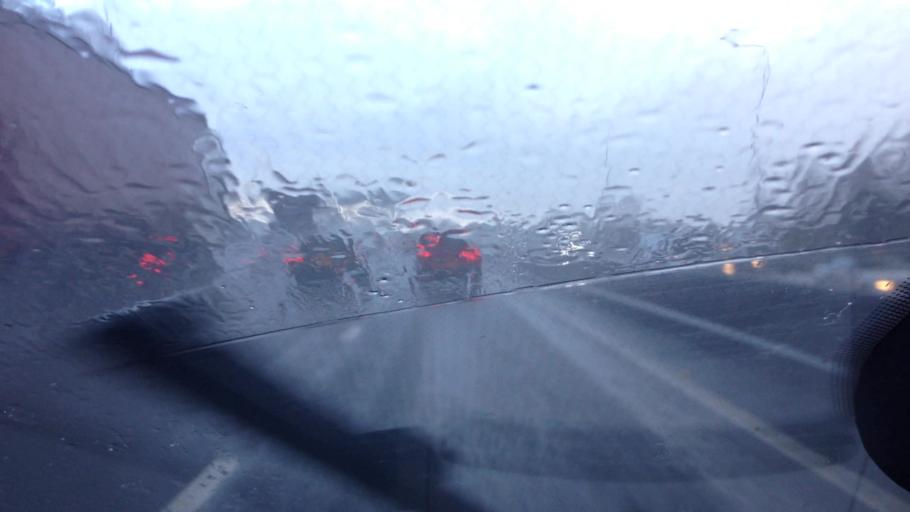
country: GB
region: England
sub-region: Kirklees
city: Cleckheaton
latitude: 53.7030
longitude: -1.7433
